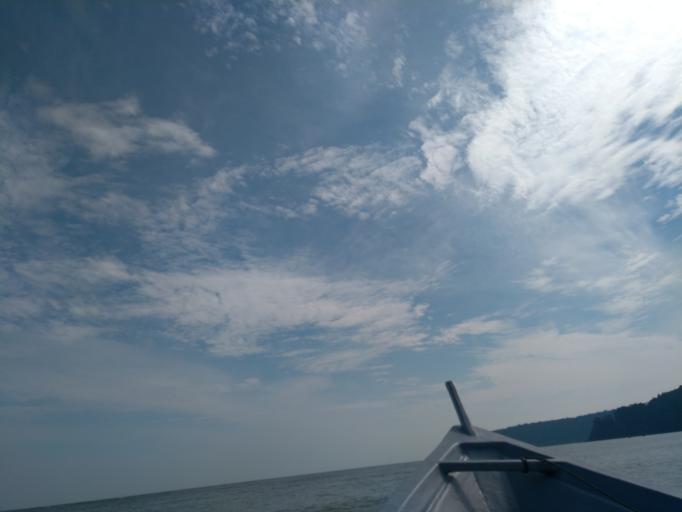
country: MY
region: Sarawak
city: Kuching
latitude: 1.7072
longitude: 110.4312
